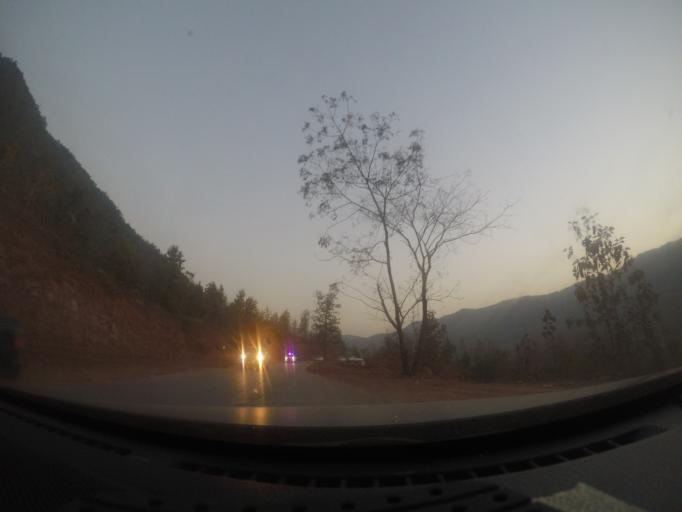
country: MM
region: Mandalay
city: Yamethin
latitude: 20.7211
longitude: 96.4993
